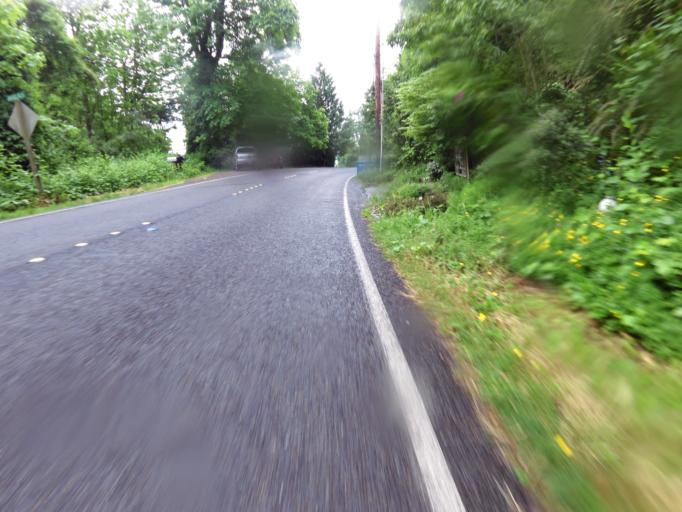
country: US
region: Washington
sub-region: King County
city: Bryn Mawr-Skyway
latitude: 47.5270
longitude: -122.2260
